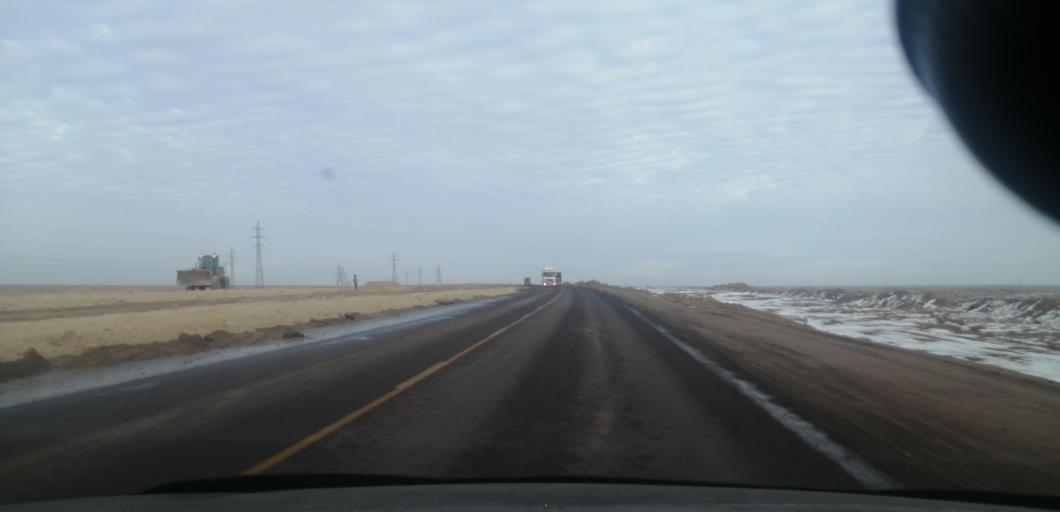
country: KZ
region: Qaraghandy
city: Balqash
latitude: 46.8034
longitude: 74.6948
